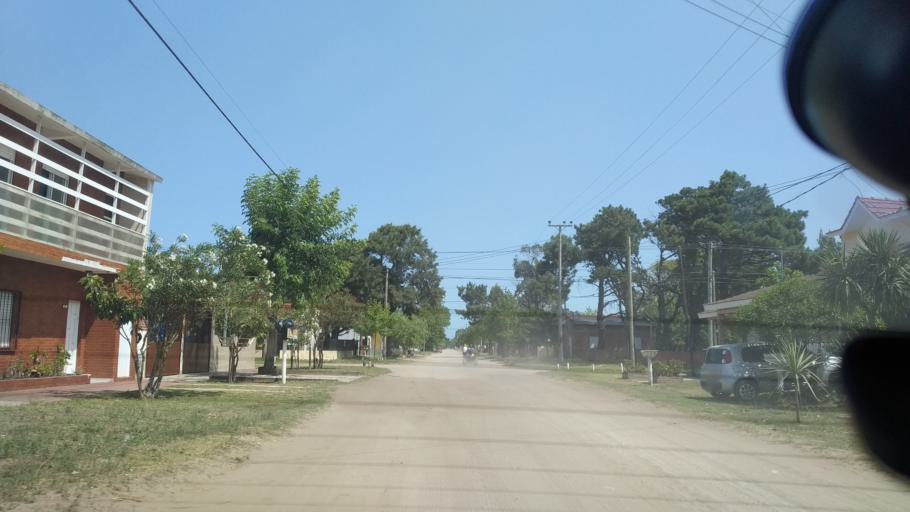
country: AR
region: Buenos Aires
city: Mar del Tuyu
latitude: -36.5831
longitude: -56.6935
